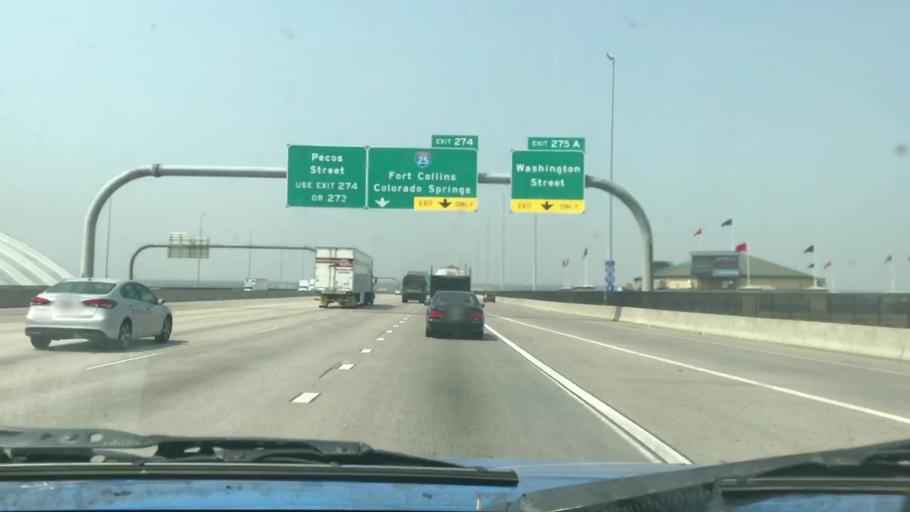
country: US
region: Colorado
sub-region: Denver County
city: Denver
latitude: 39.7801
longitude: -104.9697
